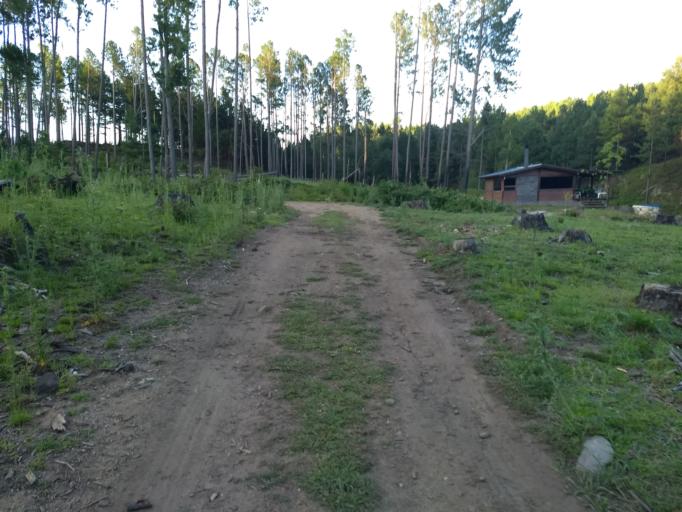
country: AR
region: Cordoba
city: Villa Berna
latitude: -31.9915
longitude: -64.8052
